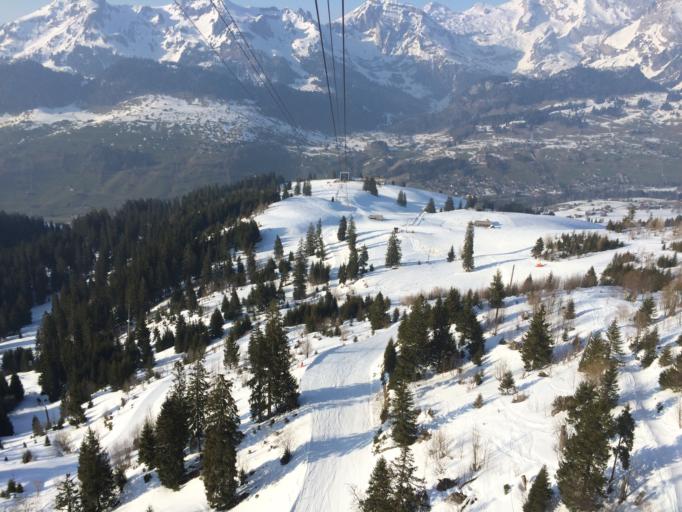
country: CH
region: Saint Gallen
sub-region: Wahlkreis Toggenburg
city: Wildhaus
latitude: 47.1763
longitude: 9.3120
